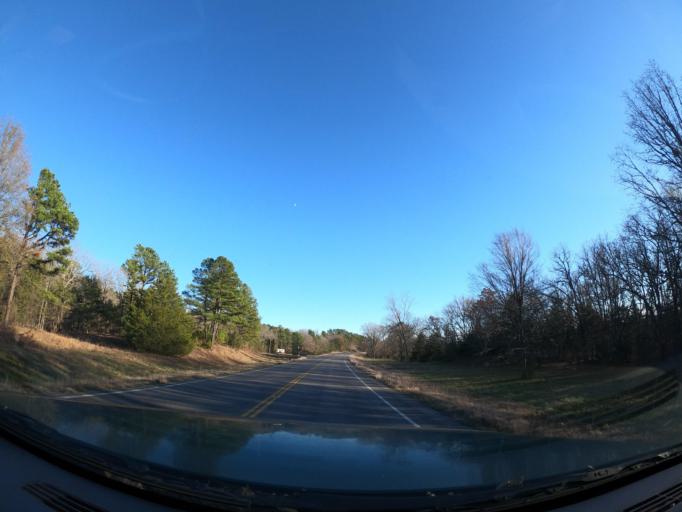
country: US
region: Oklahoma
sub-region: Latimer County
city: Wilburton
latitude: 34.9574
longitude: -95.3470
